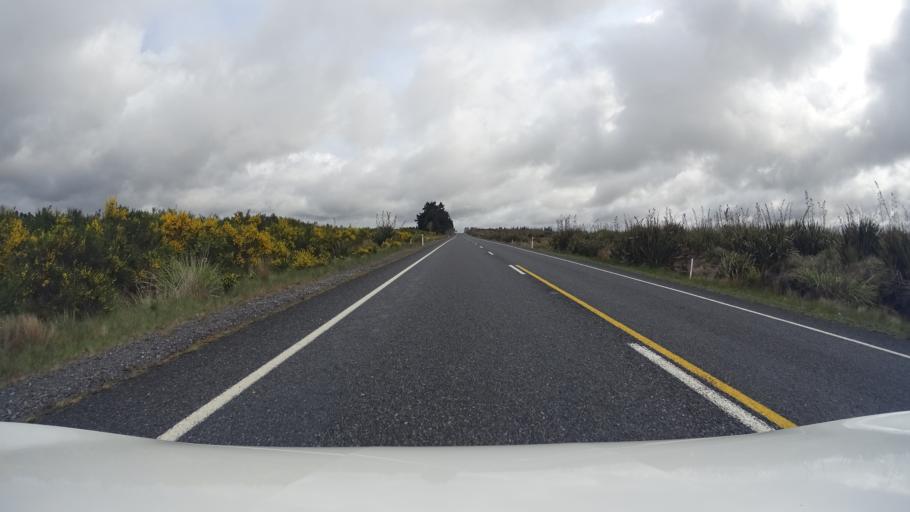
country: NZ
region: Manawatu-Wanganui
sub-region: Ruapehu District
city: Waiouru
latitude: -39.1844
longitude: 175.4020
